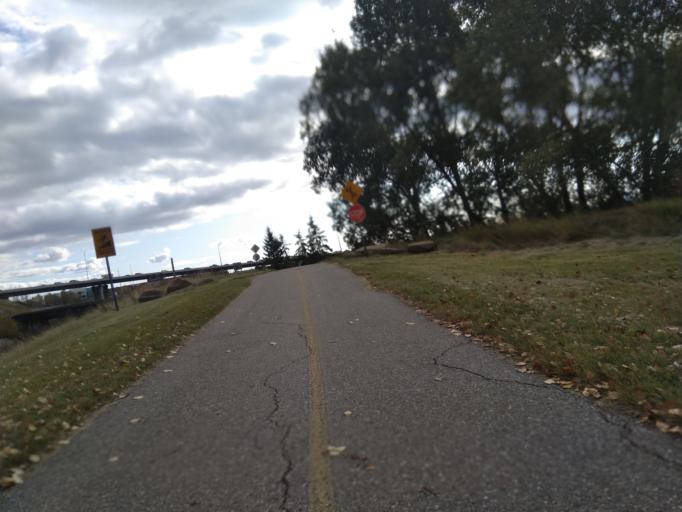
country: CA
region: Alberta
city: Calgary
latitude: 51.0136
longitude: -114.0103
